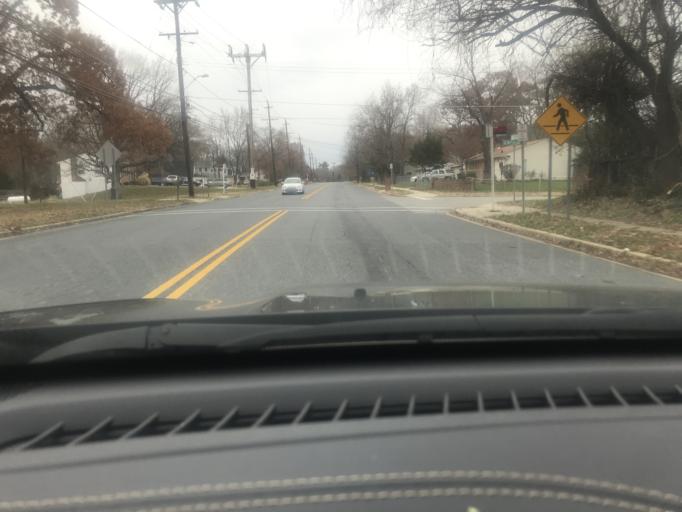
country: US
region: Maryland
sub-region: Prince George's County
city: Friendly
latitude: 38.7768
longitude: -76.9593
